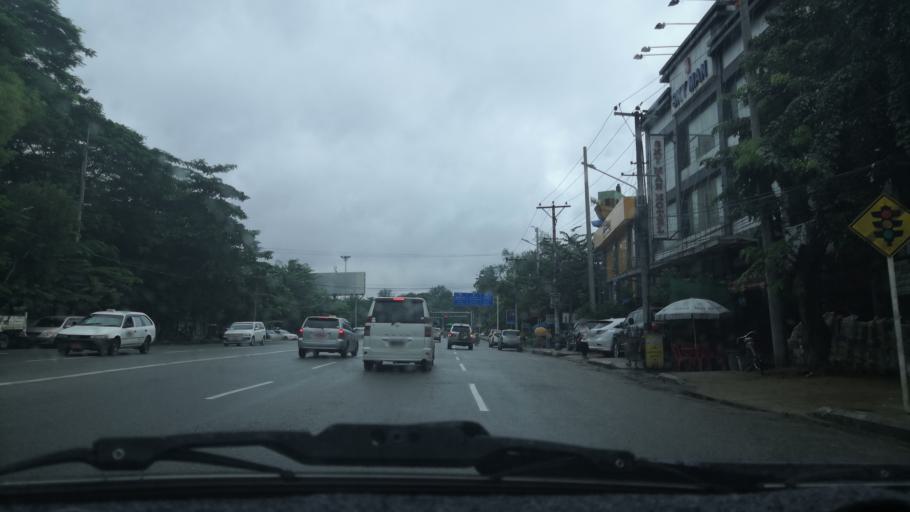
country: MM
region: Yangon
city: Yangon
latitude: 16.8887
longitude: 96.1231
